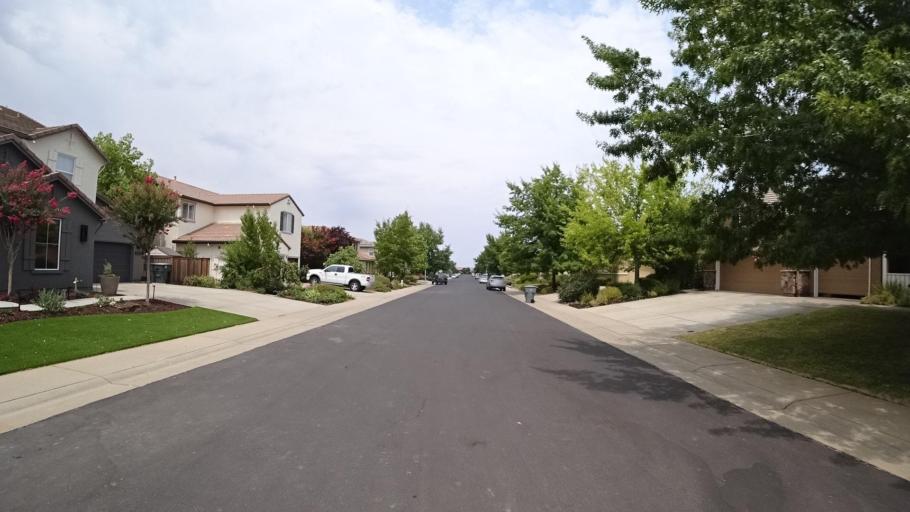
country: US
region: California
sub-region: Placer County
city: Rocklin
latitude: 38.7748
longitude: -121.2075
